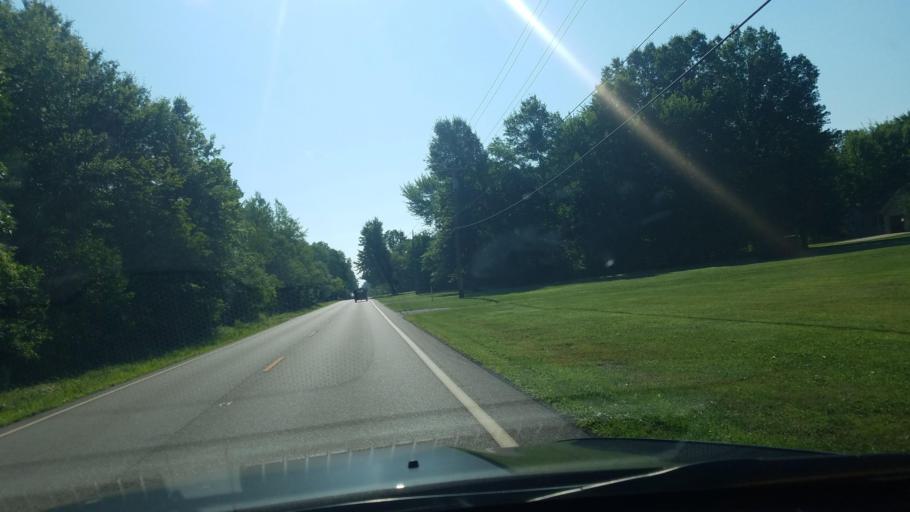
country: US
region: Ohio
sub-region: Trumbull County
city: Champion Heights
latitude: 41.3082
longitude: -80.8274
